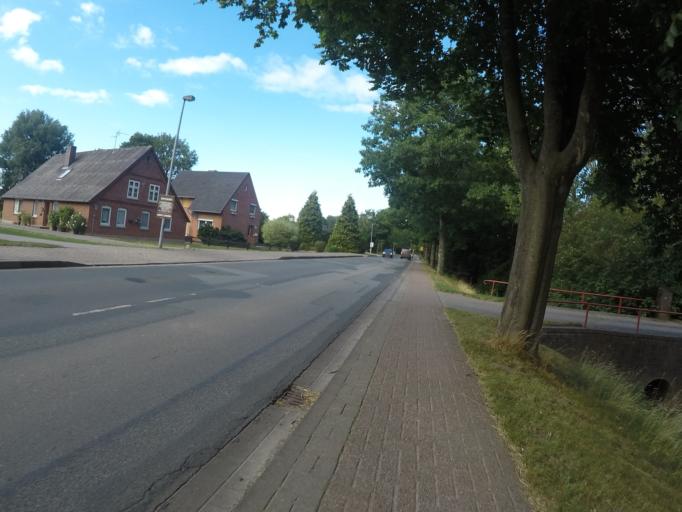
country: DE
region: Lower Saxony
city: Osterbruch
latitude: 53.7806
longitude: 8.9431
